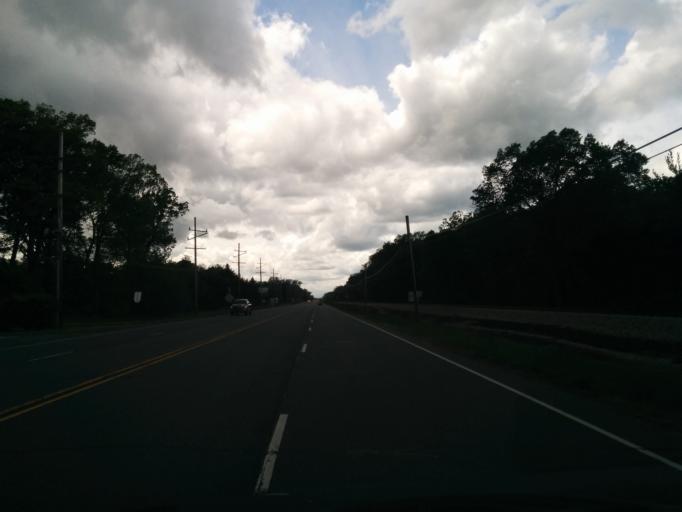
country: US
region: Indiana
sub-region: LaPorte County
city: Long Beach
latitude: 41.7413
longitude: -86.8374
